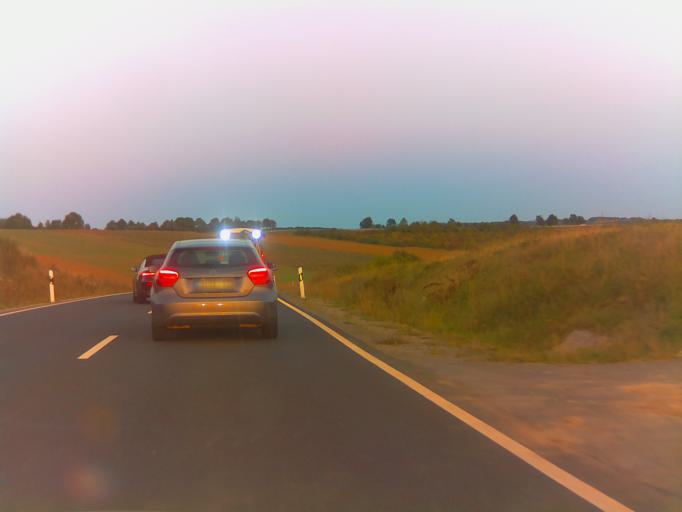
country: DE
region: Bavaria
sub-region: Regierungsbezirk Unterfranken
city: Oerlenbach
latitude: 50.1415
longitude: 10.1415
